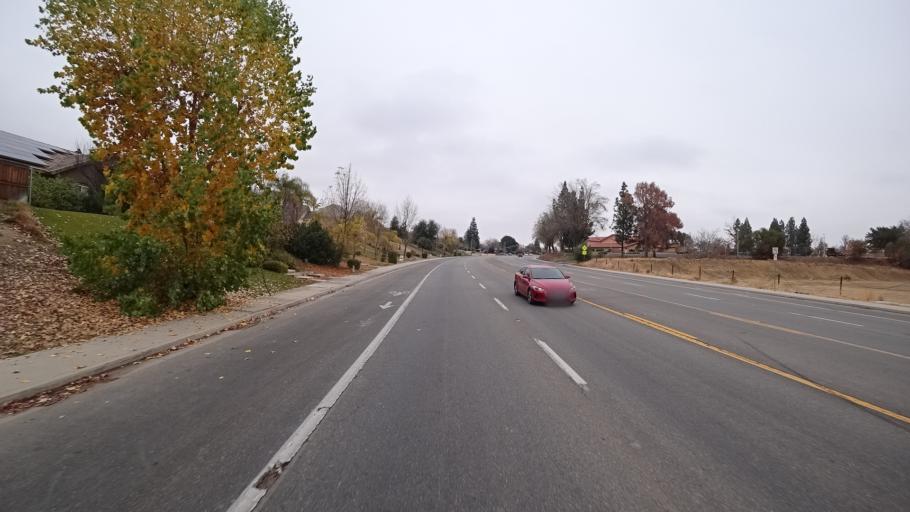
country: US
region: California
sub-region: Kern County
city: Oildale
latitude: 35.4051
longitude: -118.9306
